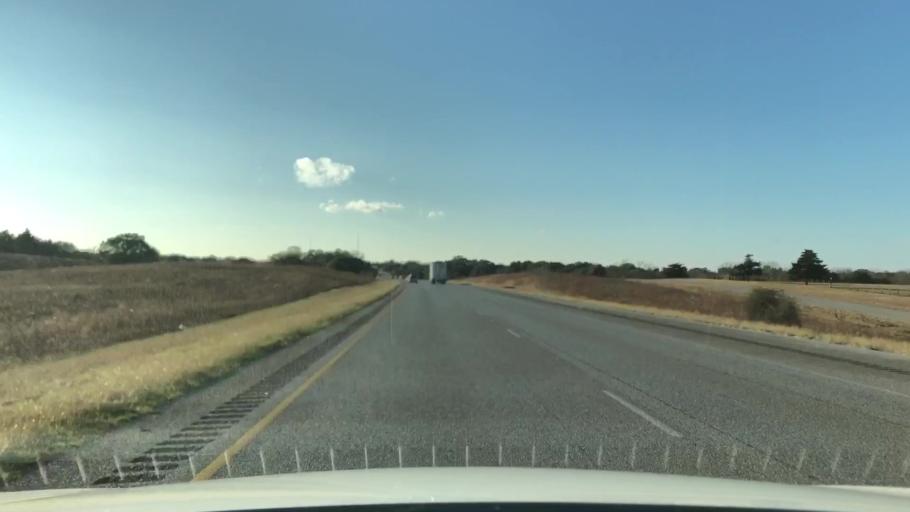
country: US
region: Texas
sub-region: Fayette County
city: Flatonia
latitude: 29.6974
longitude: -97.0410
